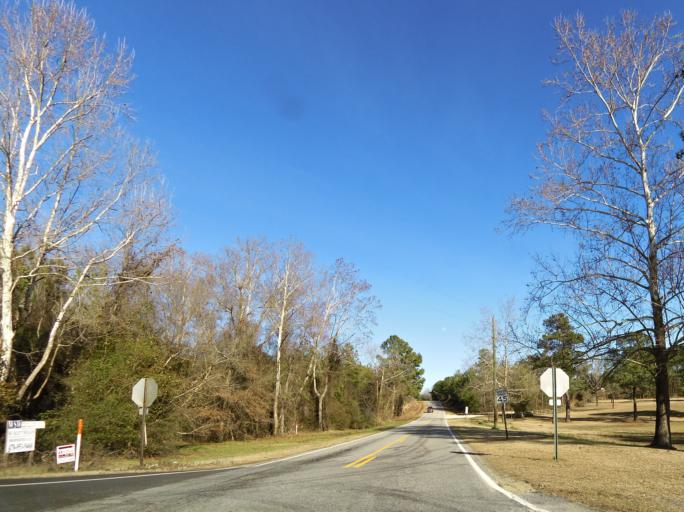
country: US
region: Georgia
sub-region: Crawford County
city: Knoxville
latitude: 32.7382
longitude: -83.9194
